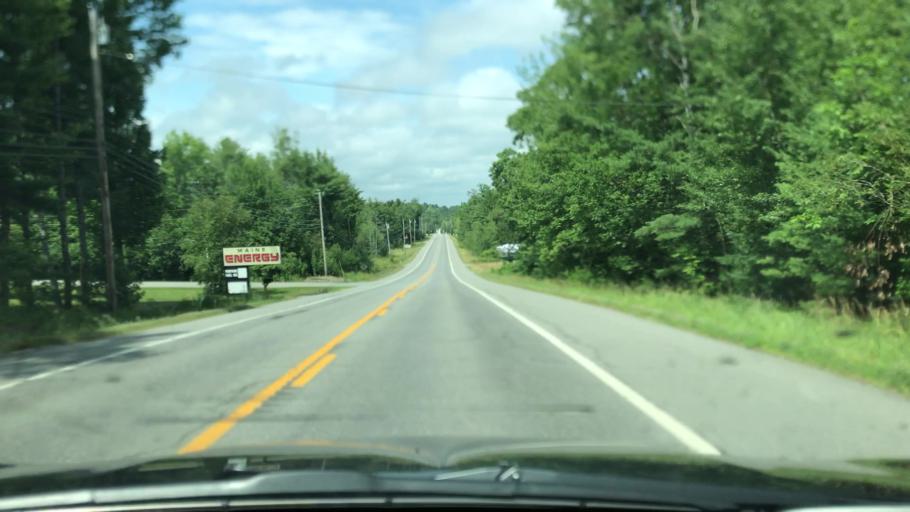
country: US
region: Maine
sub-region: Waldo County
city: Northport
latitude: 44.3743
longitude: -68.9842
